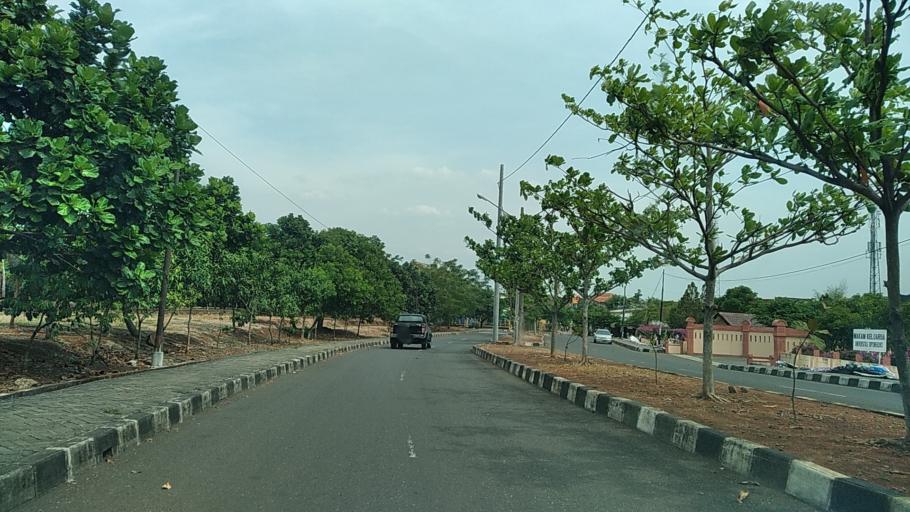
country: ID
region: Central Java
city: Semarang
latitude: -7.0480
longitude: 110.4453
